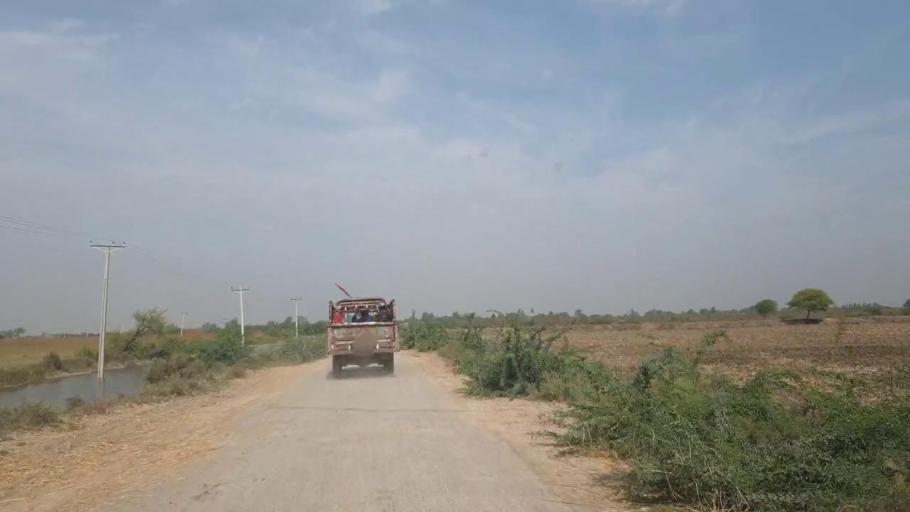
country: PK
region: Sindh
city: Tando Bago
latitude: 24.9174
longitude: 68.9948
